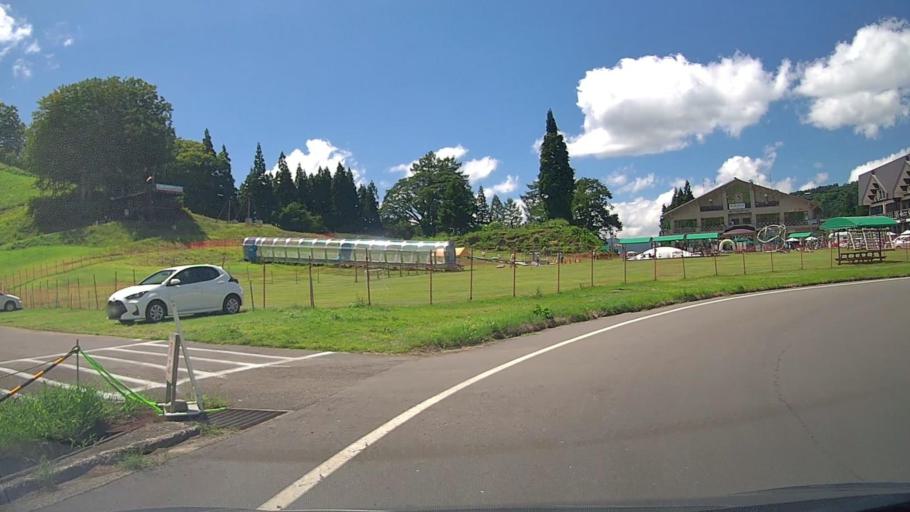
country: JP
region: Nagano
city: Iiyama
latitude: 36.9250
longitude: 138.4538
